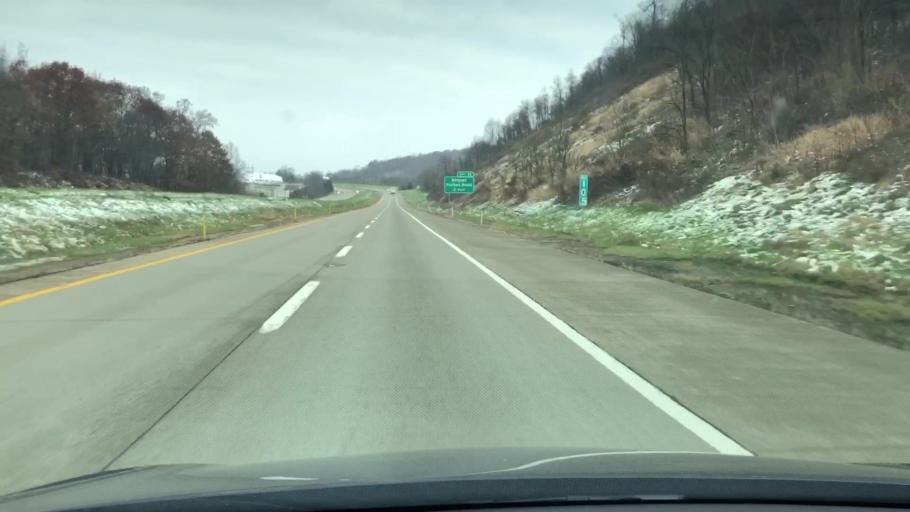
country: US
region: Pennsylvania
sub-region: Westmoreland County
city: Delmont
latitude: 40.3588
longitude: -79.5596
